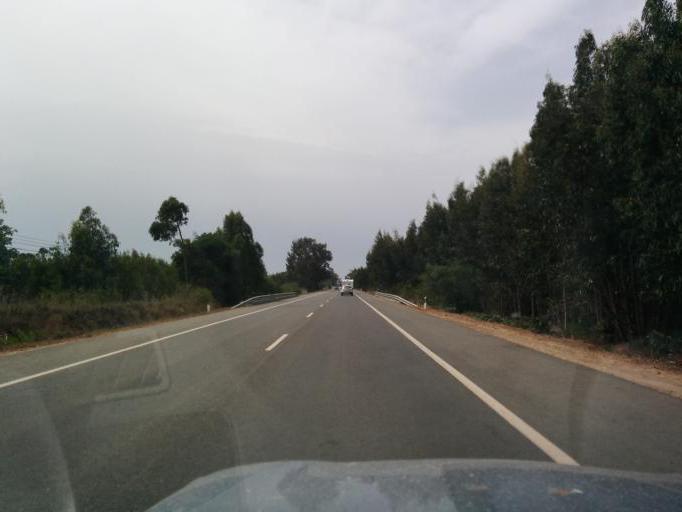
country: PT
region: Beja
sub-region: Odemira
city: Vila Nova de Milfontes
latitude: 37.7091
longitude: -8.7685
